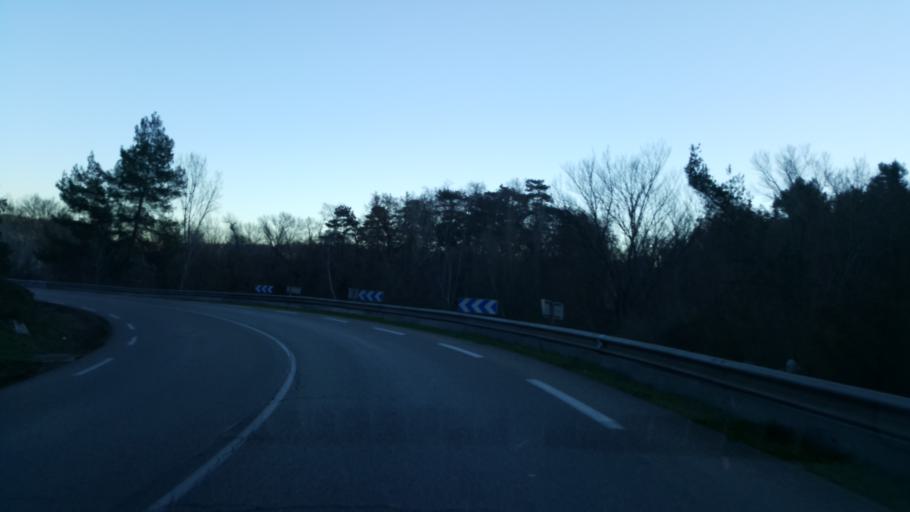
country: FR
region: Provence-Alpes-Cote d'Azur
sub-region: Departement des Bouches-du-Rhone
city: Le Tholonet
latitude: 43.5050
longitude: 5.5076
